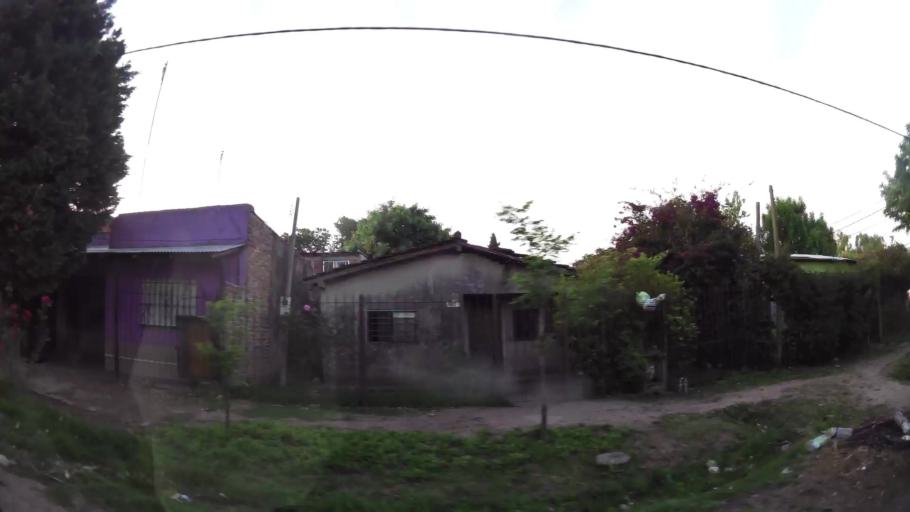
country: AR
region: Buenos Aires
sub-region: Partido de Almirante Brown
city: Adrogue
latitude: -34.7797
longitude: -58.3410
